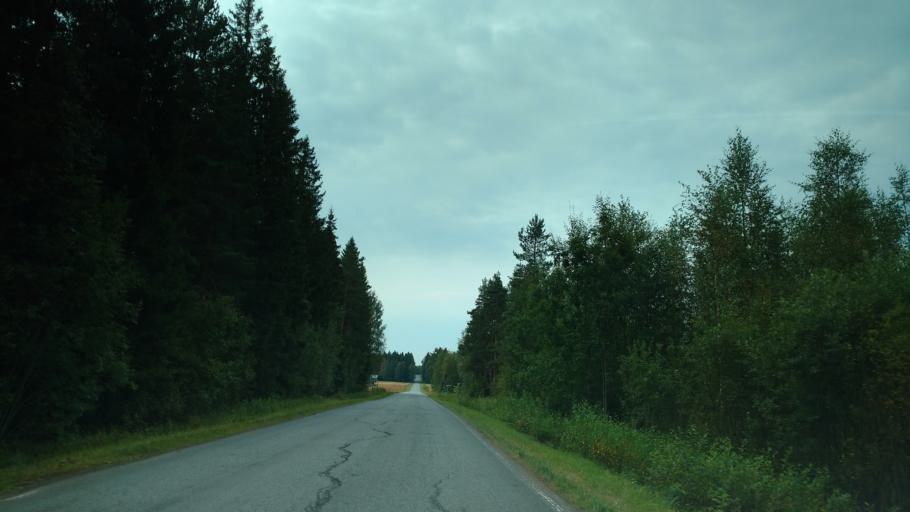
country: FI
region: Haeme
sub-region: Forssa
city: Ypaejae
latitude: 60.7601
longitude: 23.2112
